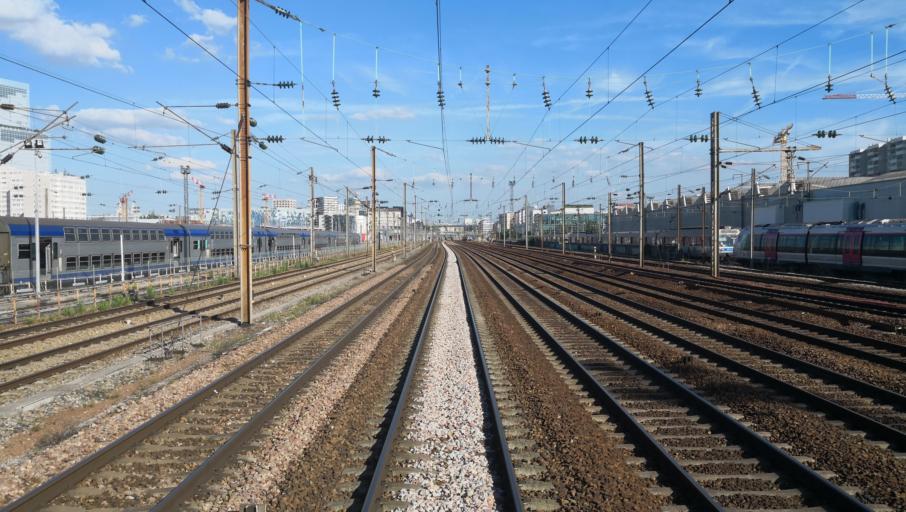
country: FR
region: Ile-de-France
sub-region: Departement des Hauts-de-Seine
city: Clichy
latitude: 48.8964
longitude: 2.3001
